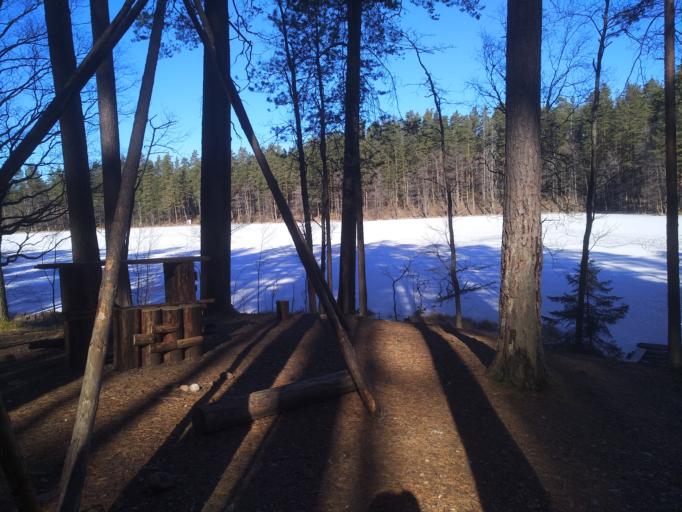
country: RU
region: Leningrad
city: Sapernoye
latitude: 60.6249
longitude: 30.0385
